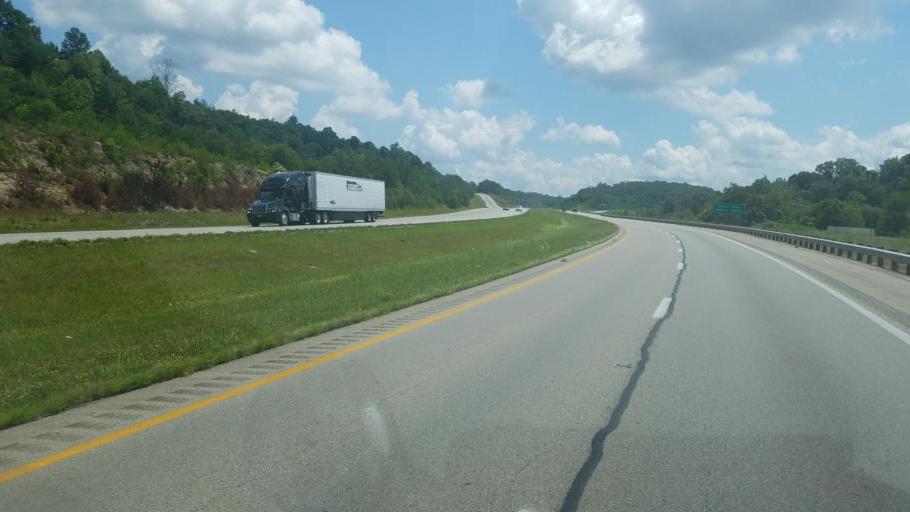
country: US
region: Ohio
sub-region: Jackson County
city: Jackson
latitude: 39.0979
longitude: -82.6678
